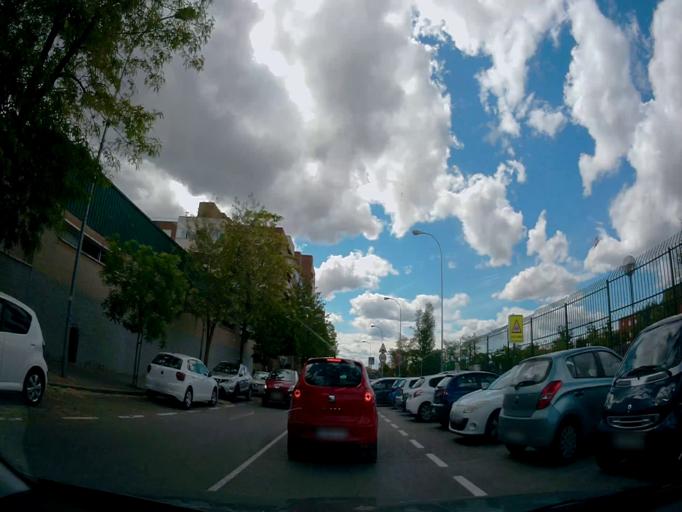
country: ES
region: Madrid
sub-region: Provincia de Madrid
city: Vicalvaro
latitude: 40.4035
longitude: -3.6185
